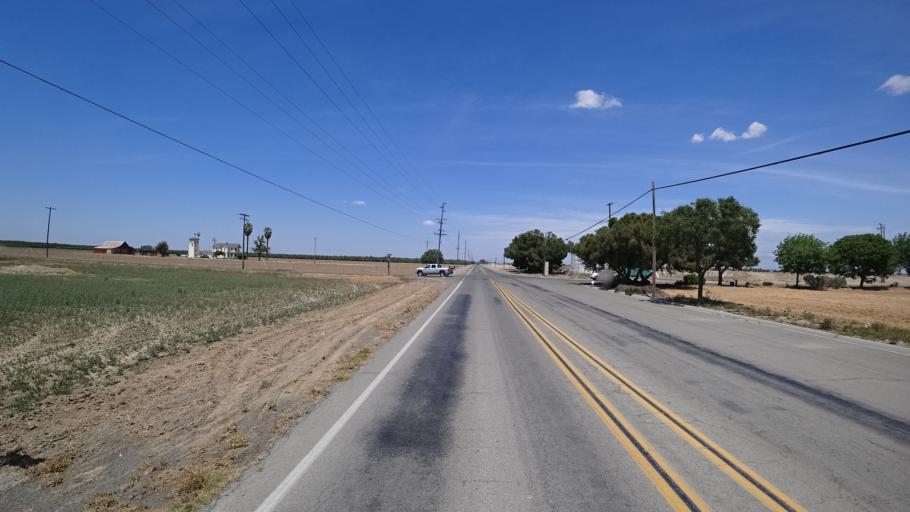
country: US
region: California
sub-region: Kings County
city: Home Garden
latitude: 36.2833
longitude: -119.6551
